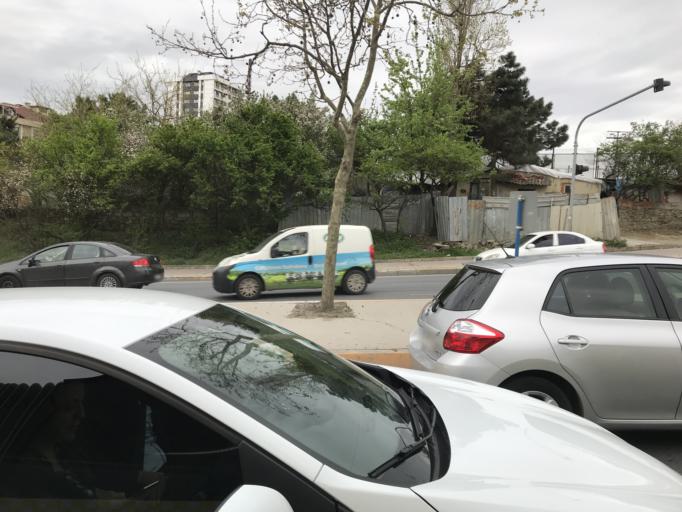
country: TR
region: Istanbul
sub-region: Atasehir
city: Atasehir
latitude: 40.9870
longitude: 29.1396
